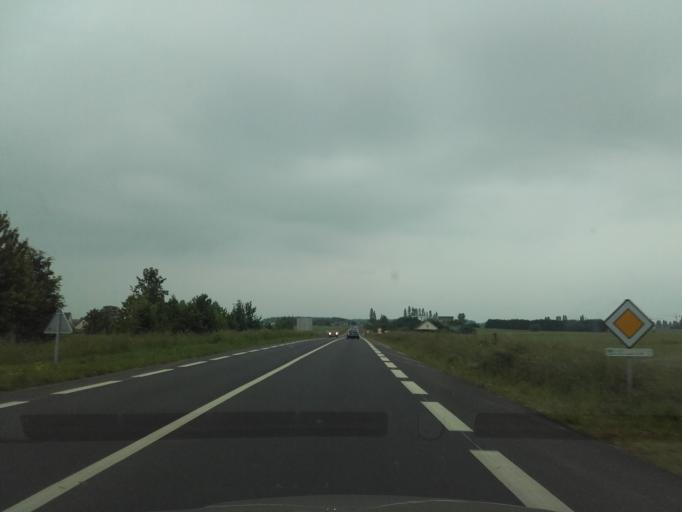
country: FR
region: Centre
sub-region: Departement d'Indre-et-Loire
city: Chanceaux-sur-Choisille
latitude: 47.4695
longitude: 0.6942
